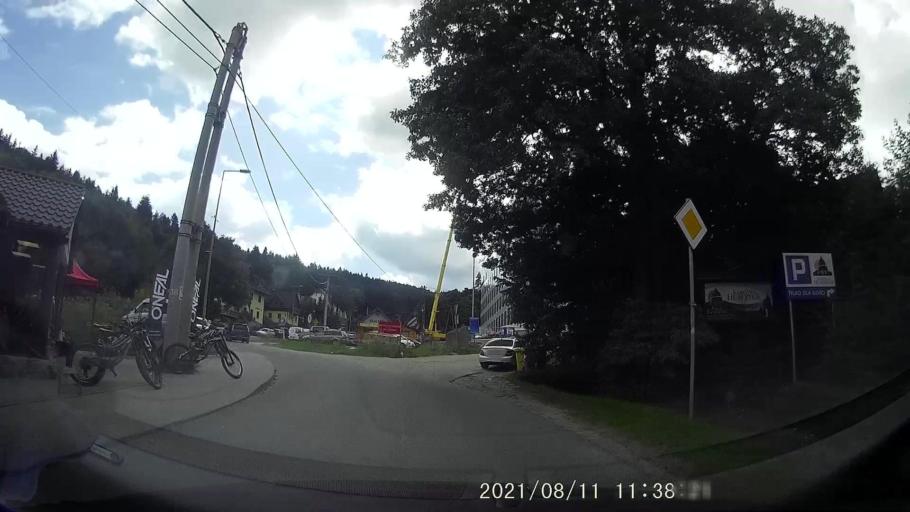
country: PL
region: Lower Silesian Voivodeship
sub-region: Powiat klodzki
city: Stronie Slaskie
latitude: 50.2593
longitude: 16.8238
